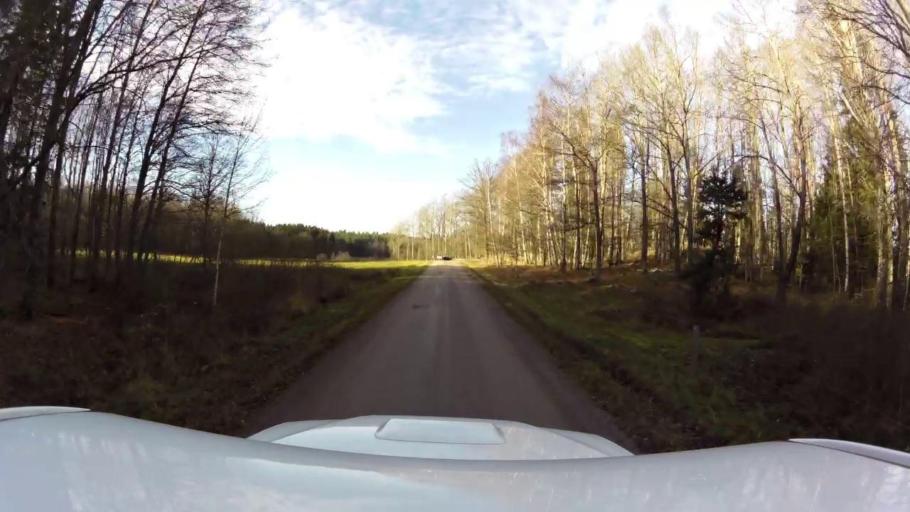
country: SE
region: OEstergoetland
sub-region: Linkopings Kommun
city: Linkoping
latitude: 58.3565
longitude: 15.6113
